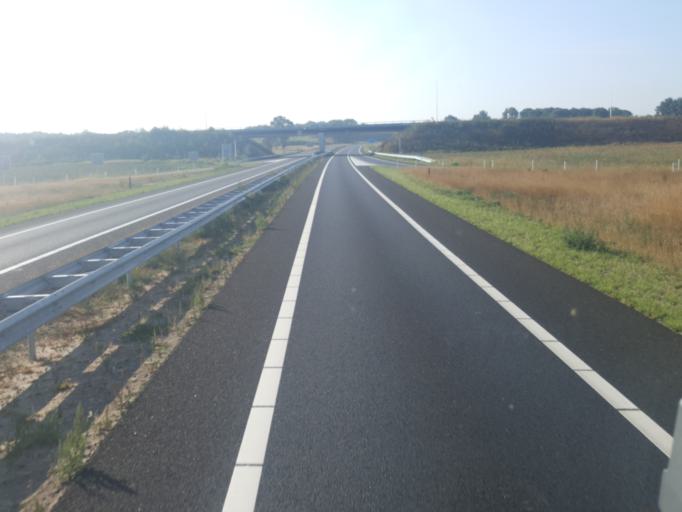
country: NL
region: Gelderland
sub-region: Berkelland
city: Eibergen
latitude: 52.0877
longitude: 6.6306
